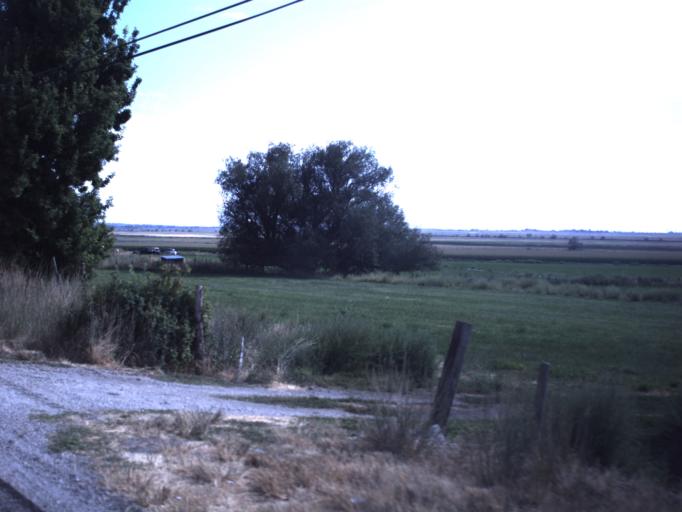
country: US
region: Utah
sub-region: Box Elder County
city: Honeyville
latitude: 41.5900
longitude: -112.0440
